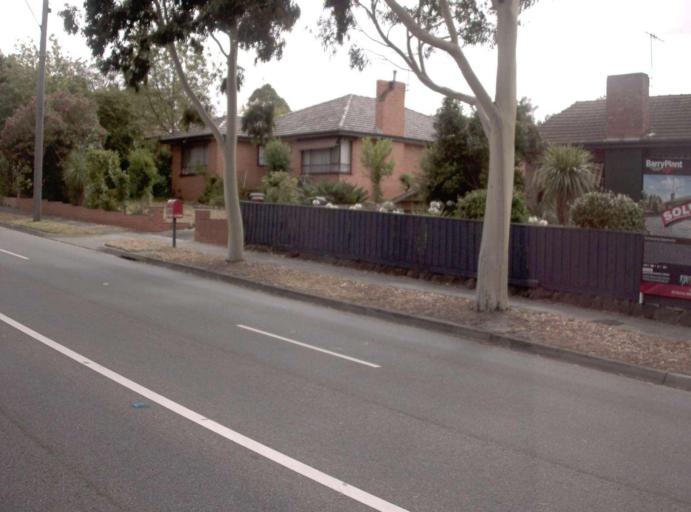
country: AU
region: Victoria
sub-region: Monash
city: Ashwood
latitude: -37.8651
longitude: 145.1122
